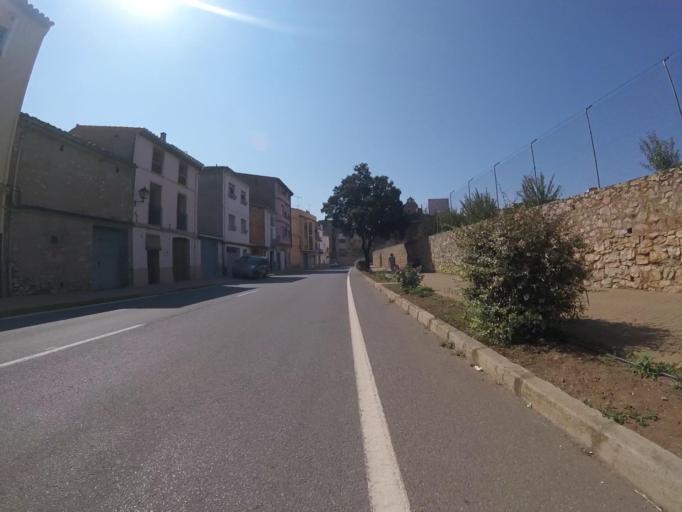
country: ES
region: Valencia
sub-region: Provincia de Castello
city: Adzaneta
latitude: 40.2180
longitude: -0.1703
